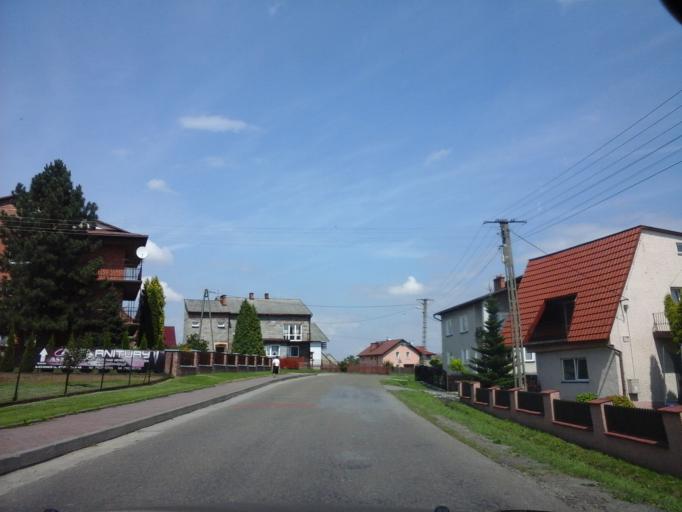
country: PL
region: Lesser Poland Voivodeship
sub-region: Powiat wadowicki
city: Bachowice
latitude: 49.9673
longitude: 19.4939
